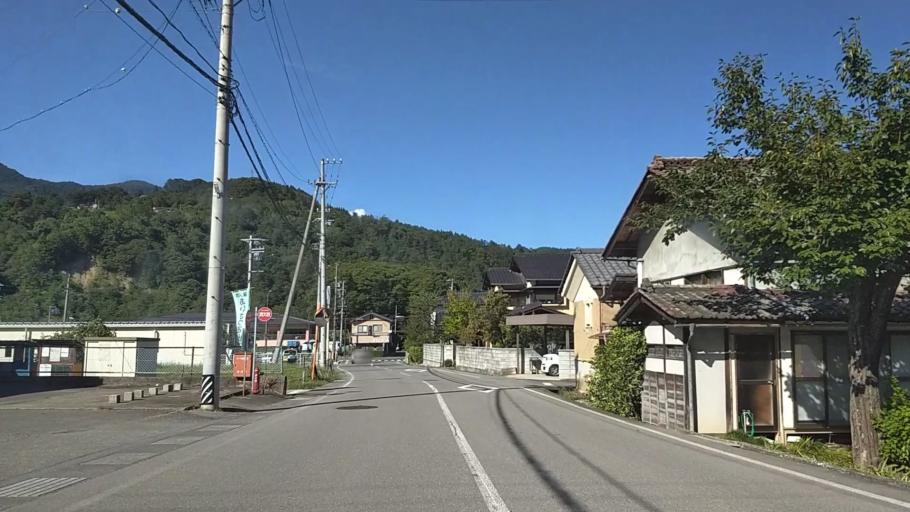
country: JP
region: Nagano
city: Nagano-shi
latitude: 36.6160
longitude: 138.0953
